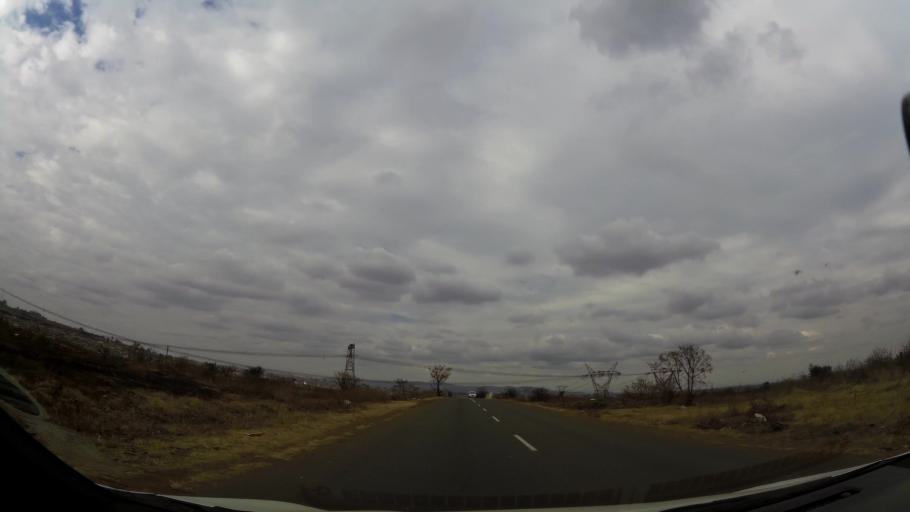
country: ZA
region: Gauteng
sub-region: Ekurhuleni Metropolitan Municipality
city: Germiston
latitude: -26.3772
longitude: 28.1093
